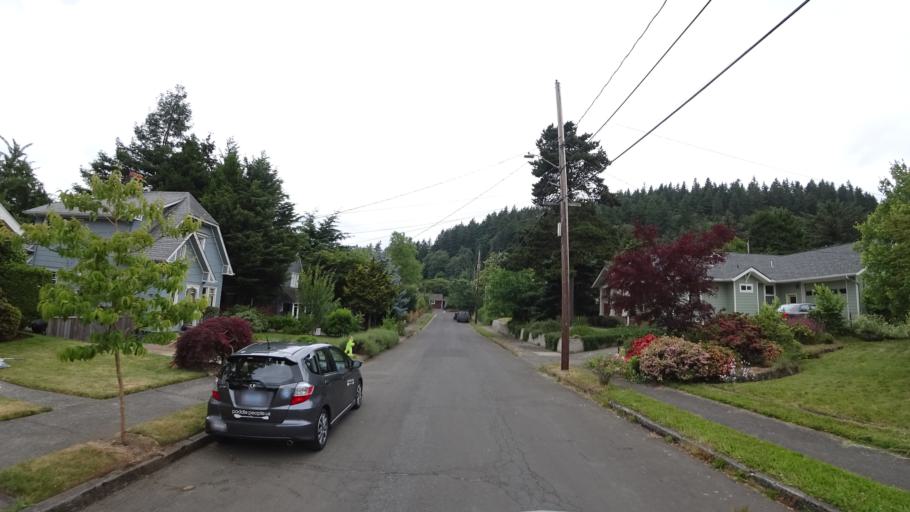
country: US
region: Oregon
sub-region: Multnomah County
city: Lents
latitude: 45.5086
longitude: -122.5876
